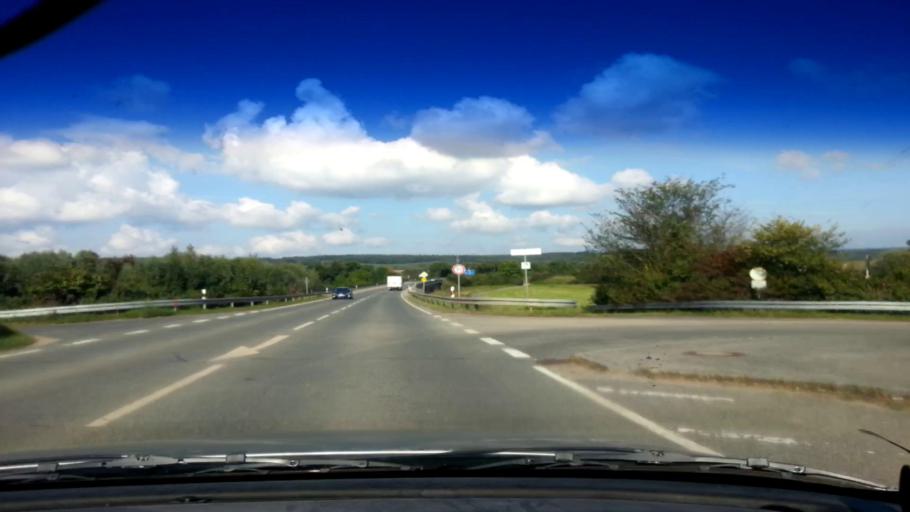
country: DE
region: Bavaria
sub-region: Upper Franconia
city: Viereth-Trunstadt
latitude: 49.9262
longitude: 10.7686
